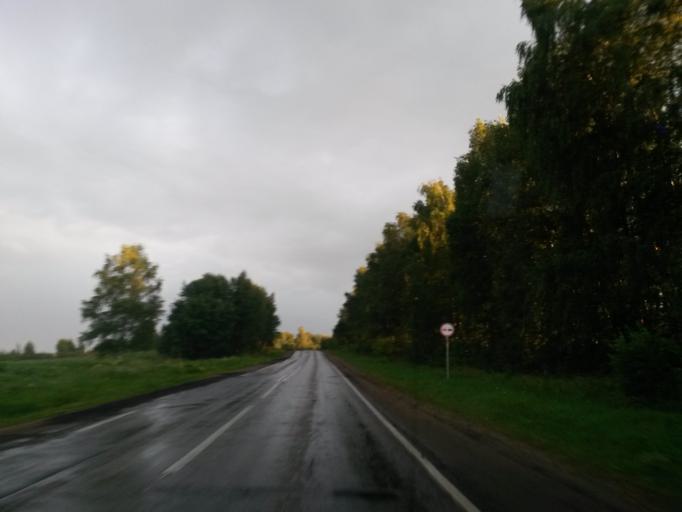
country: RU
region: Jaroslavl
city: Yaroslavl
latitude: 57.5468
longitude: 39.8618
